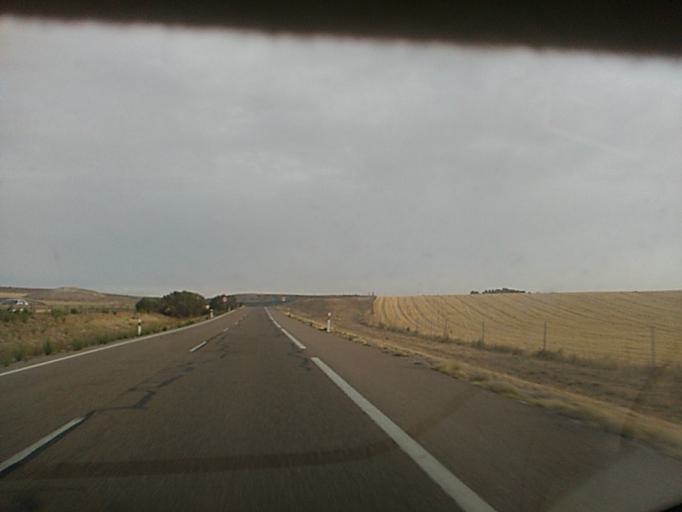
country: ES
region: Castille and Leon
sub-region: Provincia de Valladolid
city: Mota del Marques
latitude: 41.6579
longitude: -5.1941
